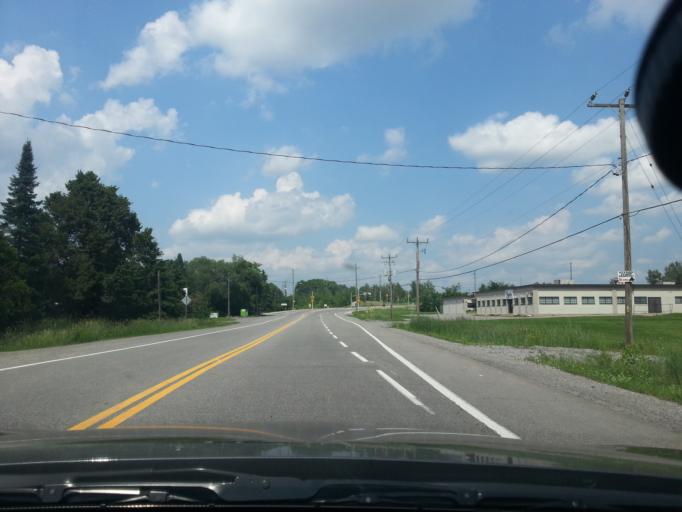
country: CA
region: Ontario
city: Ottawa
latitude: 45.3192
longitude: -75.6910
